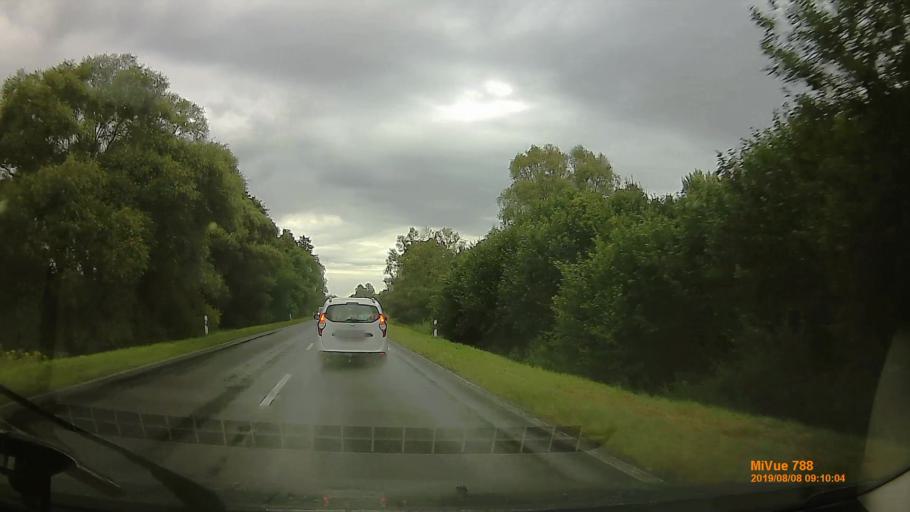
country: HU
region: Zala
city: Zalaegerszeg
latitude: 46.7658
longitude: 16.8576
